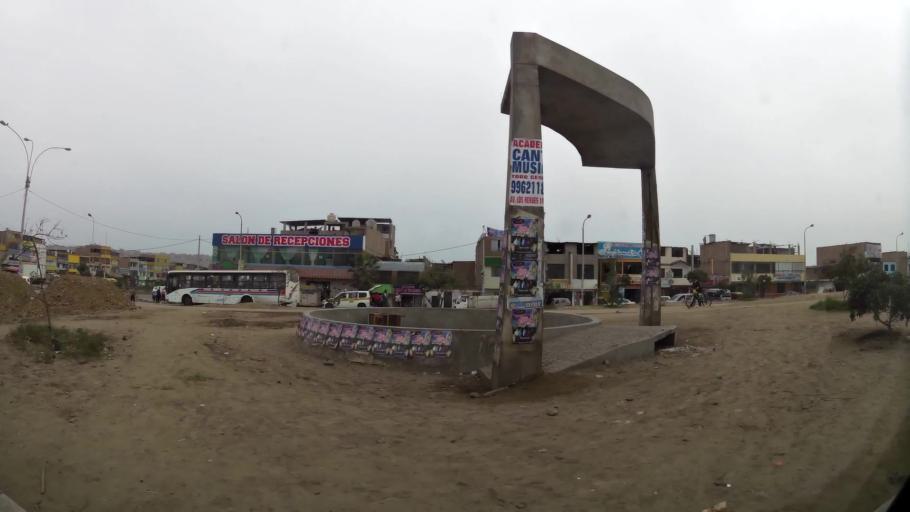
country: PE
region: Lima
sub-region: Lima
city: Surco
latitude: -12.2253
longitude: -76.9410
